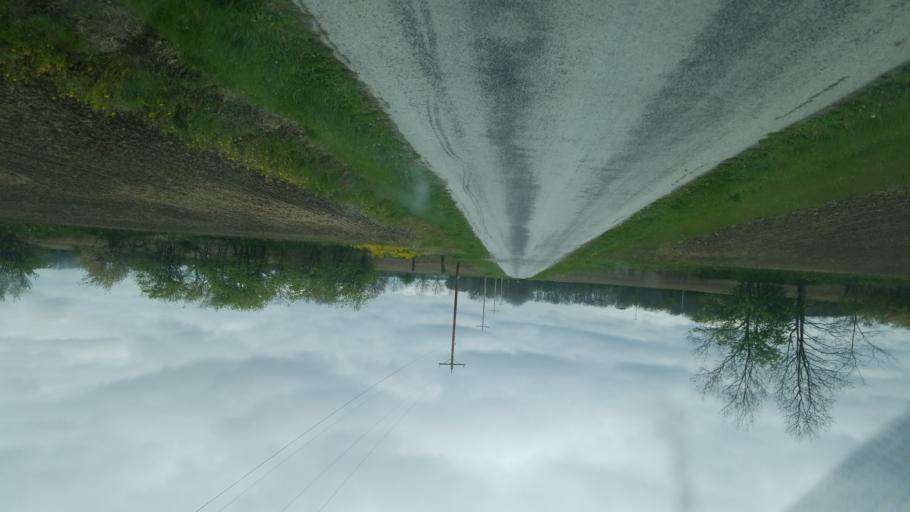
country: US
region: Ohio
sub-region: Hardin County
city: Kenton
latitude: 40.7246
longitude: -83.5849
